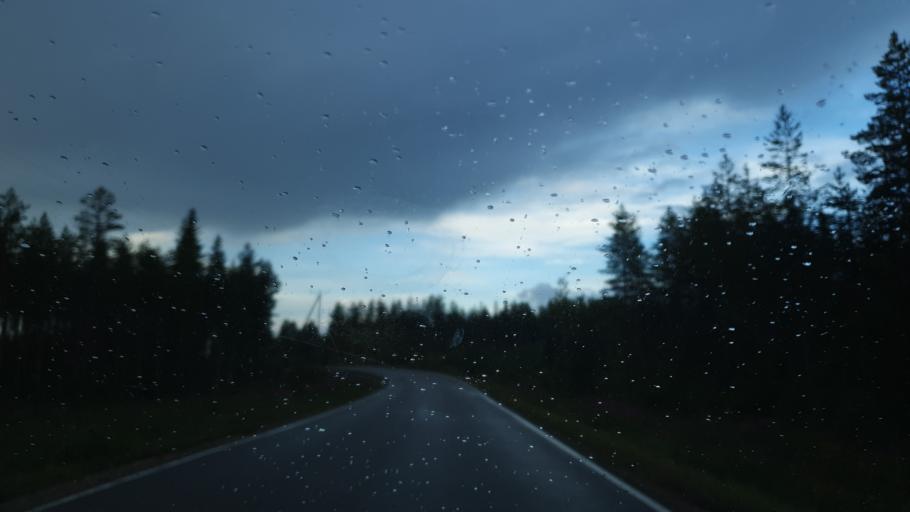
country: FI
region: North Karelia
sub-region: Pielisen Karjala
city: Lieksa
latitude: 63.6611
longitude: 29.8691
